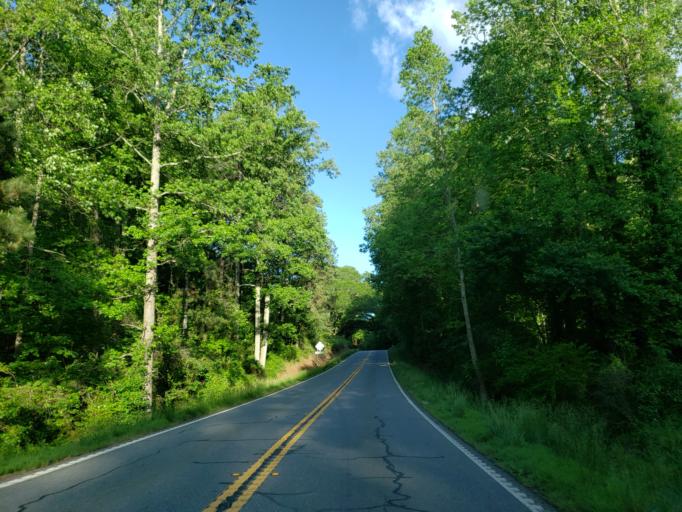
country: US
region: Georgia
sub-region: Bartow County
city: Rydal
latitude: 34.3488
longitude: -84.5909
